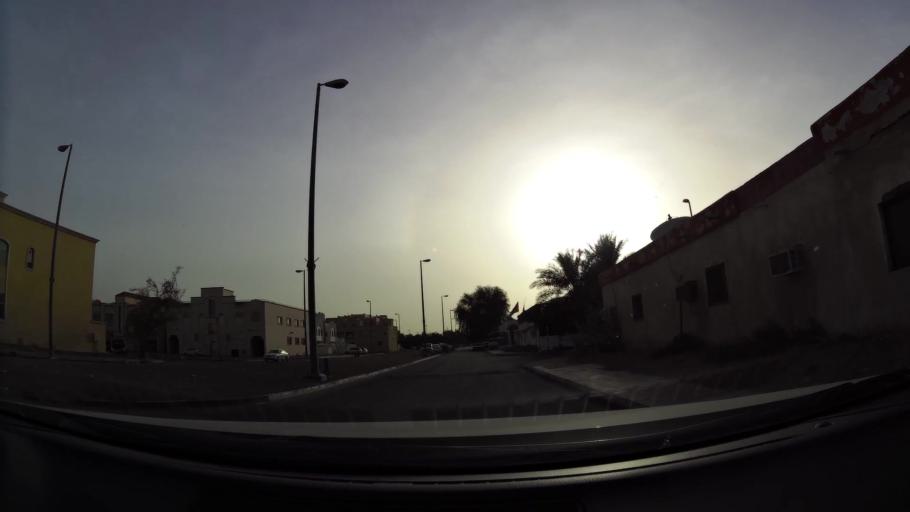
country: OM
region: Al Buraimi
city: Al Buraymi
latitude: 24.2429
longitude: 55.7429
